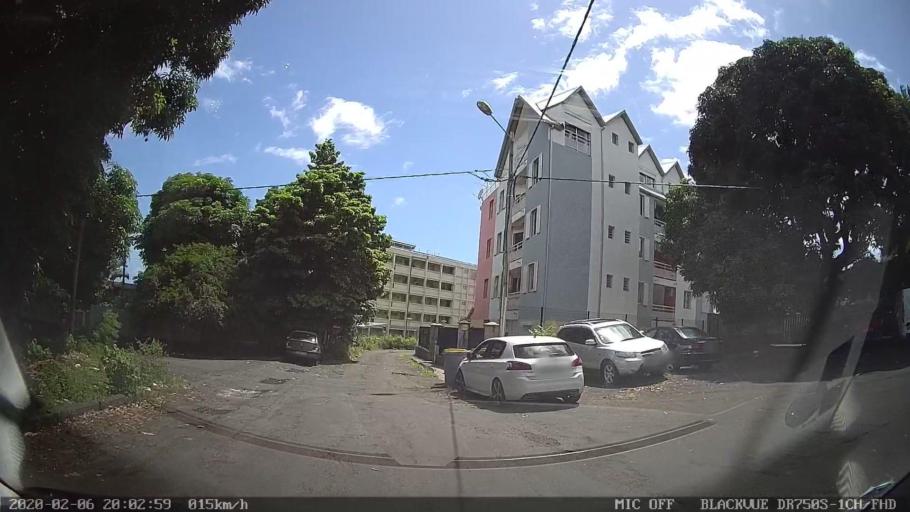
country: RE
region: Reunion
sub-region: Reunion
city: Saint-Denis
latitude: -20.8962
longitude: 55.4619
